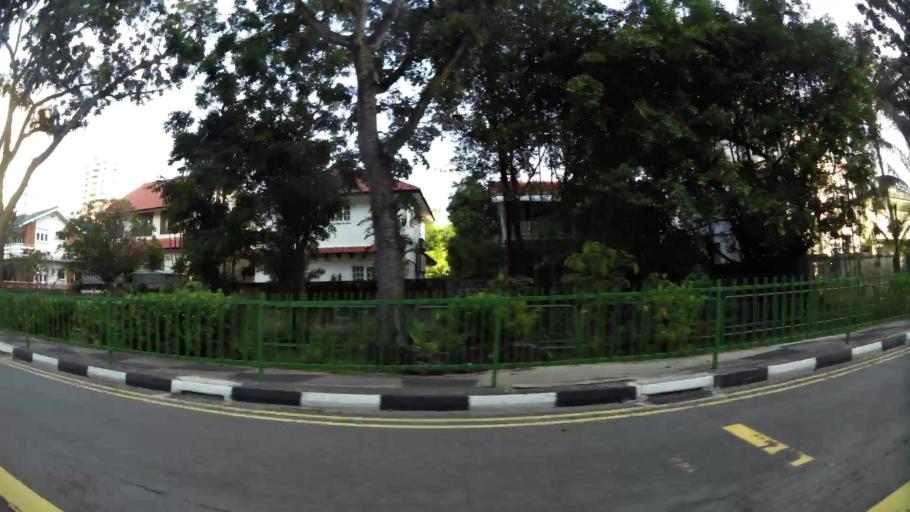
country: SG
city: Singapore
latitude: 1.3080
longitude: 103.9206
